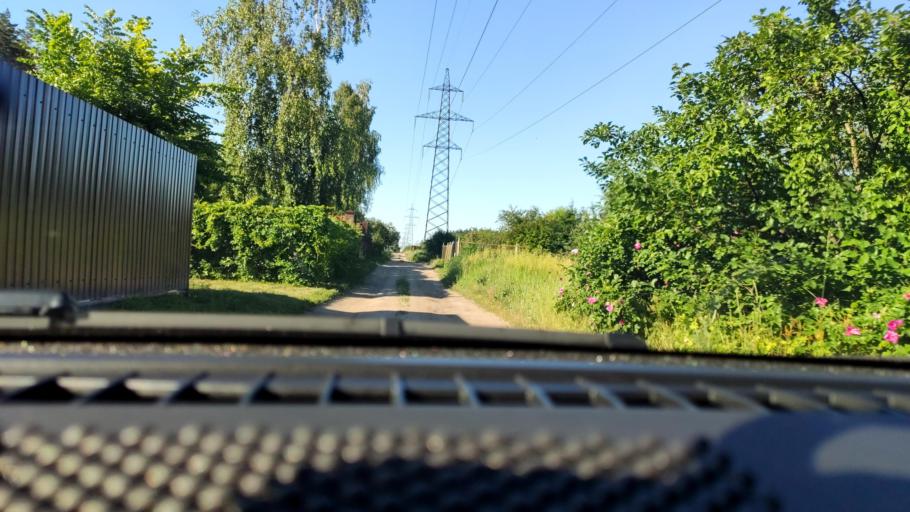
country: RU
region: Voronezj
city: Volya
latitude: 51.7449
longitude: 39.4615
